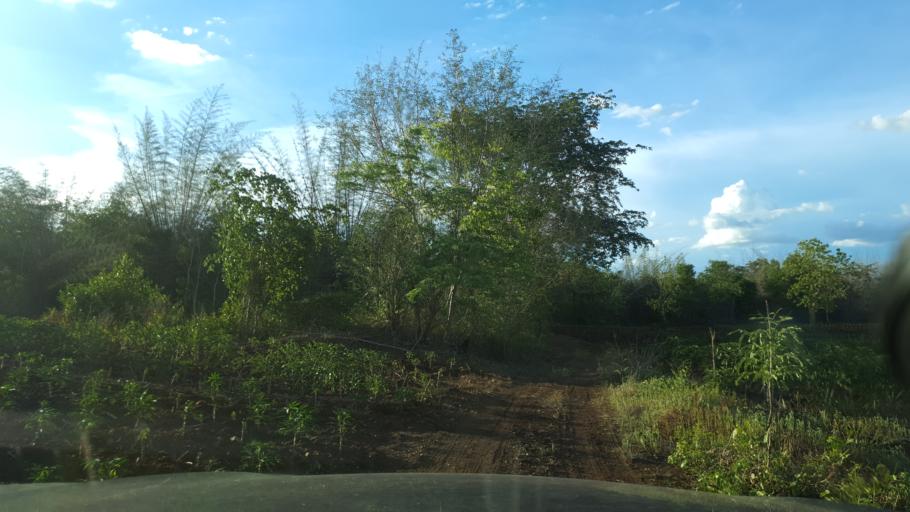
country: TH
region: Lampang
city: Sop Prap
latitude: 17.9621
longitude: 99.3520
